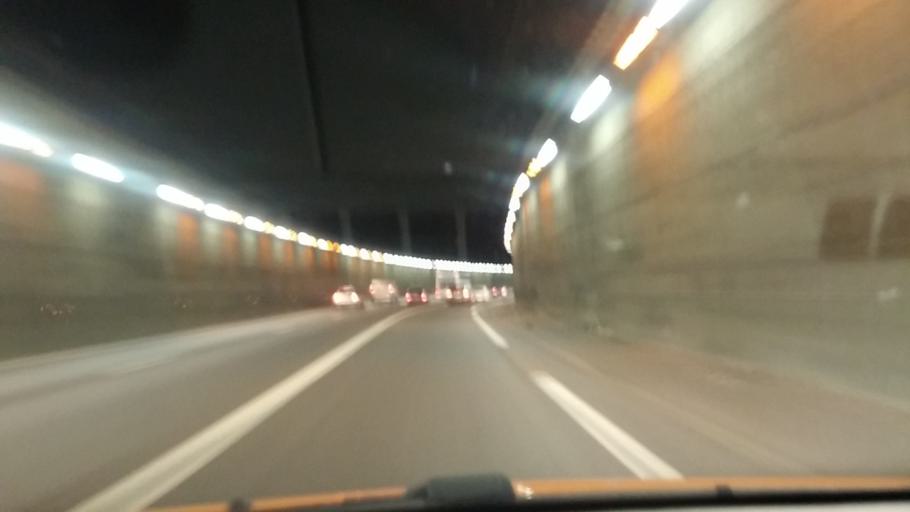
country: FR
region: Ile-de-France
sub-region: Departement du Val-de-Marne
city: Nogent-sur-Marne
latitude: 48.8394
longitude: 2.4933
